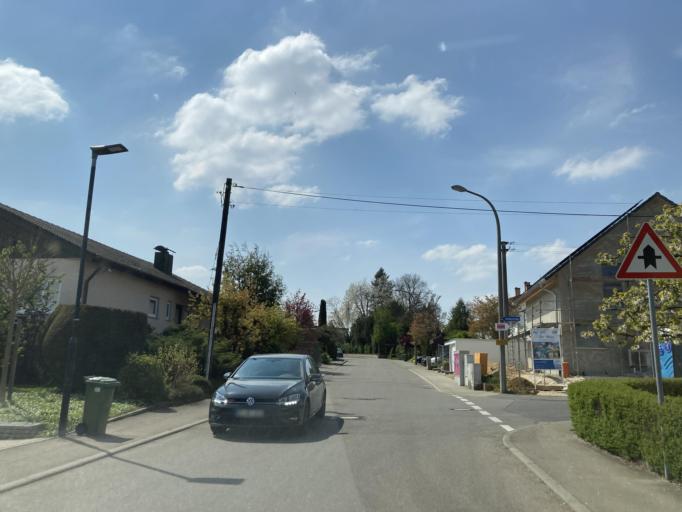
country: DE
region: Baden-Wuerttemberg
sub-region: Tuebingen Region
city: Kusterdingen
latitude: 48.5208
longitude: 9.1133
